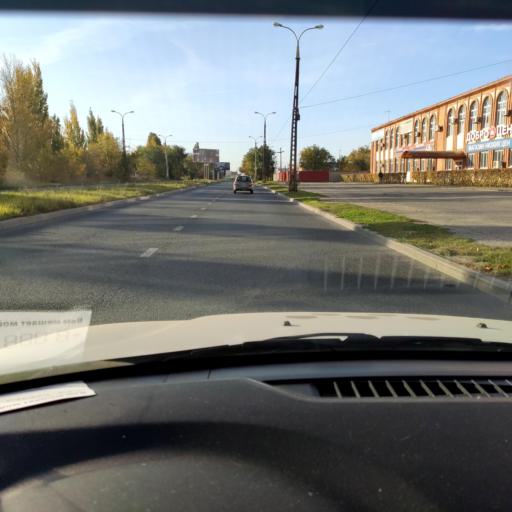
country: RU
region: Samara
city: Tol'yatti
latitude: 53.5574
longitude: 49.3043
